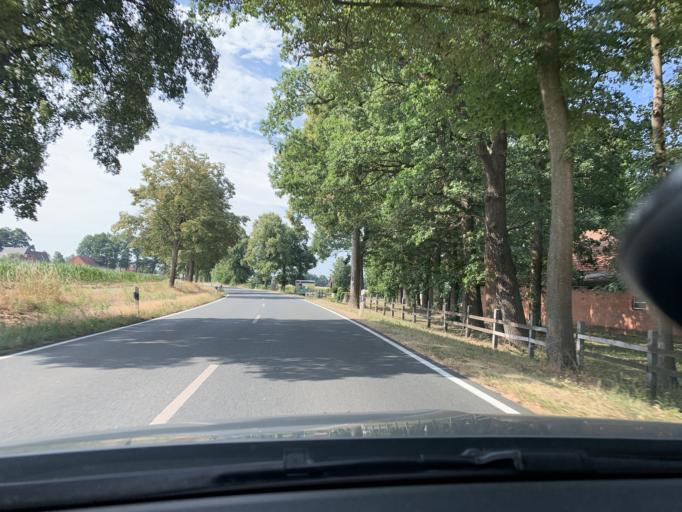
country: DE
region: North Rhine-Westphalia
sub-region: Regierungsbezirk Detmold
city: Langenberg
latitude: 51.7478
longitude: 8.3814
